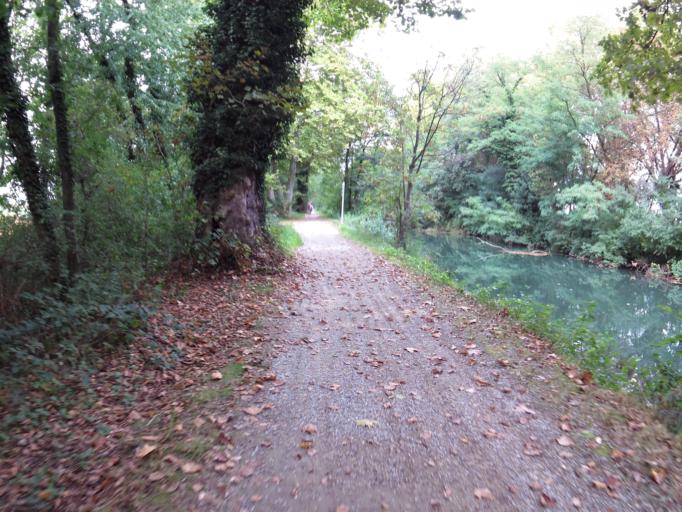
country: FR
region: Alsace
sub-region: Departement du Bas-Rhin
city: Marckolsheim
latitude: 48.1509
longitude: 7.5346
